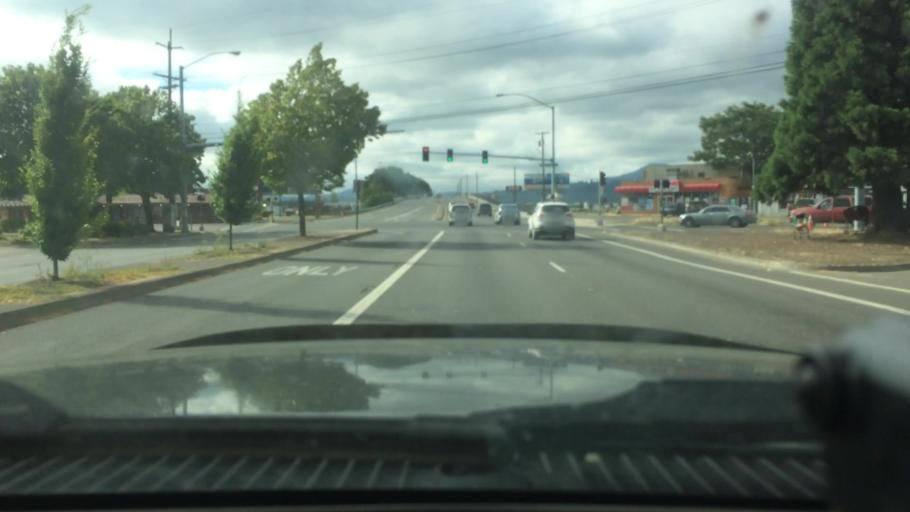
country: US
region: Oregon
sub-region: Lane County
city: Eugene
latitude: 44.0642
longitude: -123.1374
